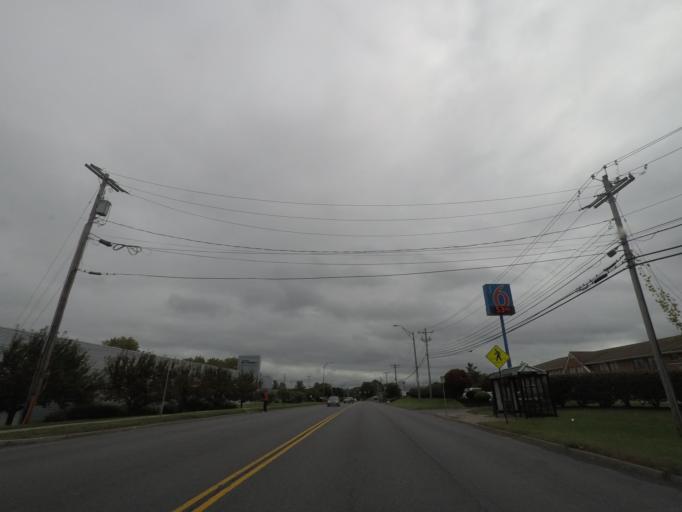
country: US
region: New York
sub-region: Albany County
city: West Albany
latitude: 42.6799
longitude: -73.7833
